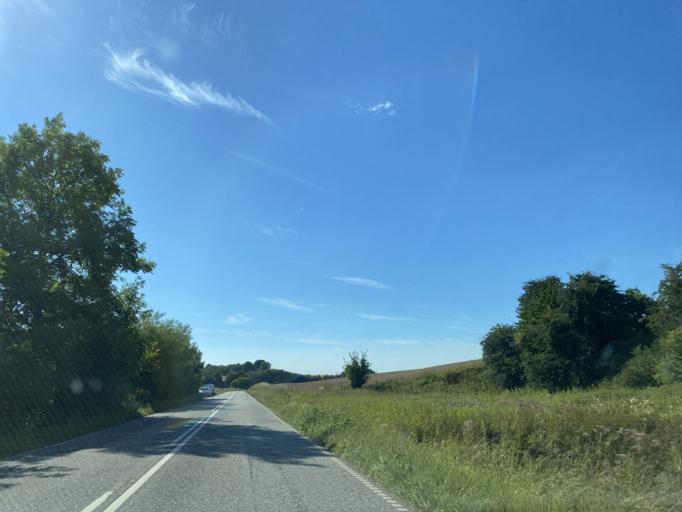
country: DK
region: Central Jutland
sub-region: Hedensted Kommune
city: Torring
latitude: 55.8239
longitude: 9.4468
